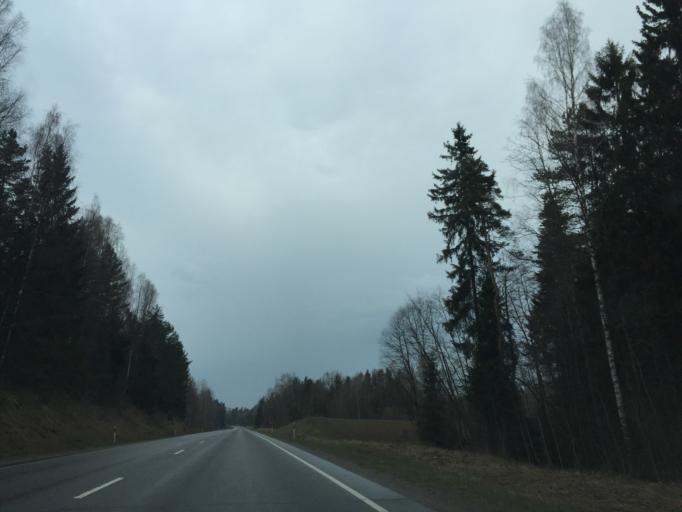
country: EE
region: Tartu
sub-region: UElenurme vald
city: Ulenurme
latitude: 58.1166
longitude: 26.7342
